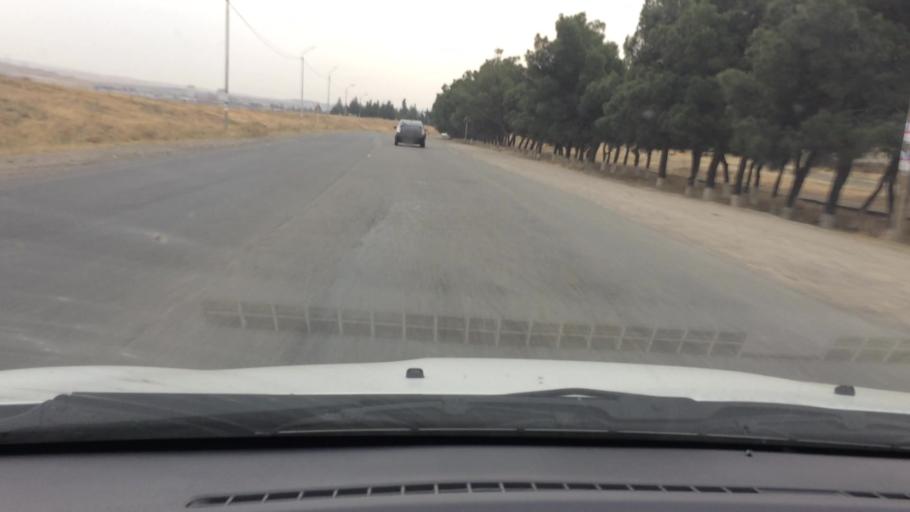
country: GE
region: Kvemo Kartli
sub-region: Marneuli
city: Marneuli
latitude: 41.5048
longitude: 44.7986
